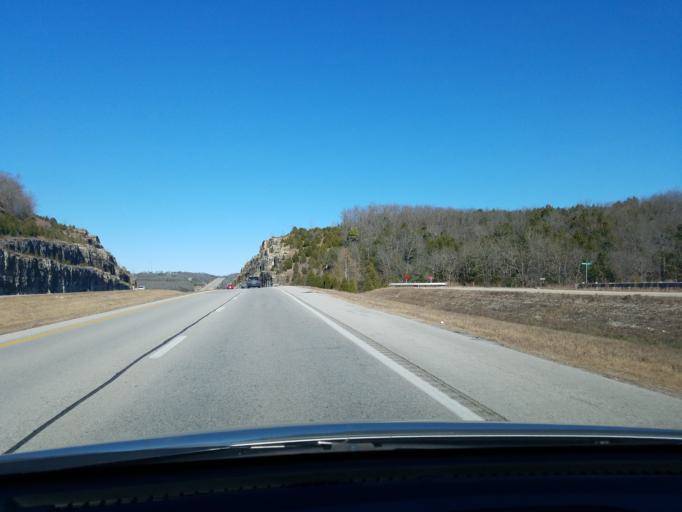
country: US
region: Missouri
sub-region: Taney County
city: Merriam Woods
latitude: 36.7598
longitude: -93.2225
